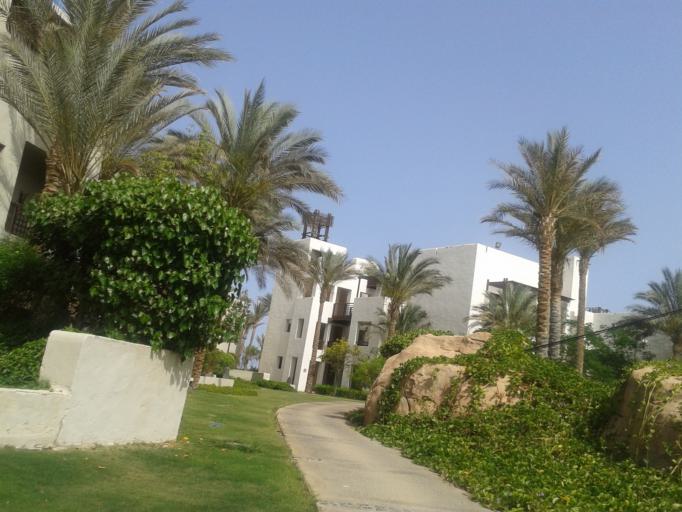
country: EG
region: Red Sea
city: Marsa Alam
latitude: 25.5396
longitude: 34.6397
